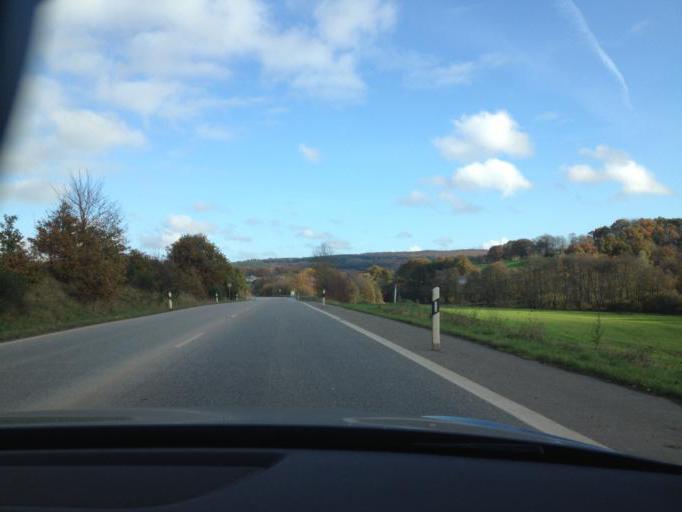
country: DE
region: Saarland
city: Sankt Wendel
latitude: 49.4514
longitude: 7.1602
